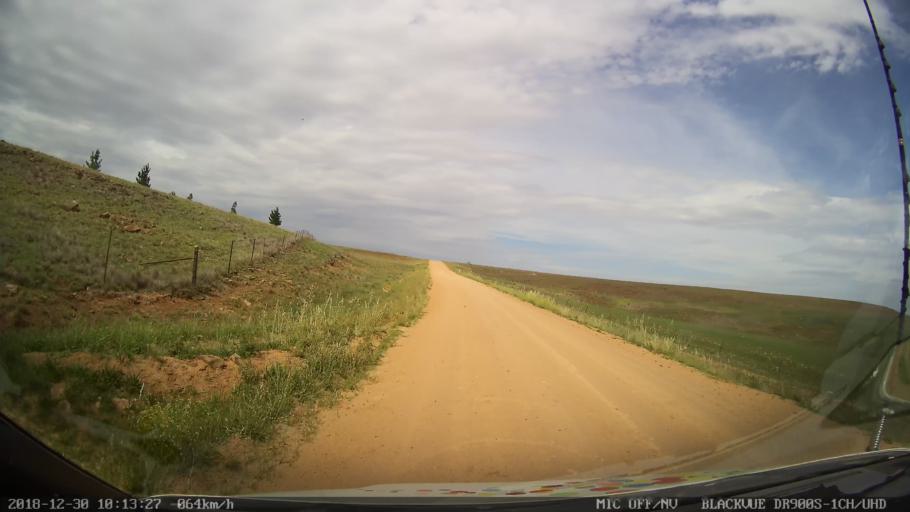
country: AU
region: New South Wales
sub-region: Snowy River
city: Berridale
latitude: -36.5378
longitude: 149.0654
